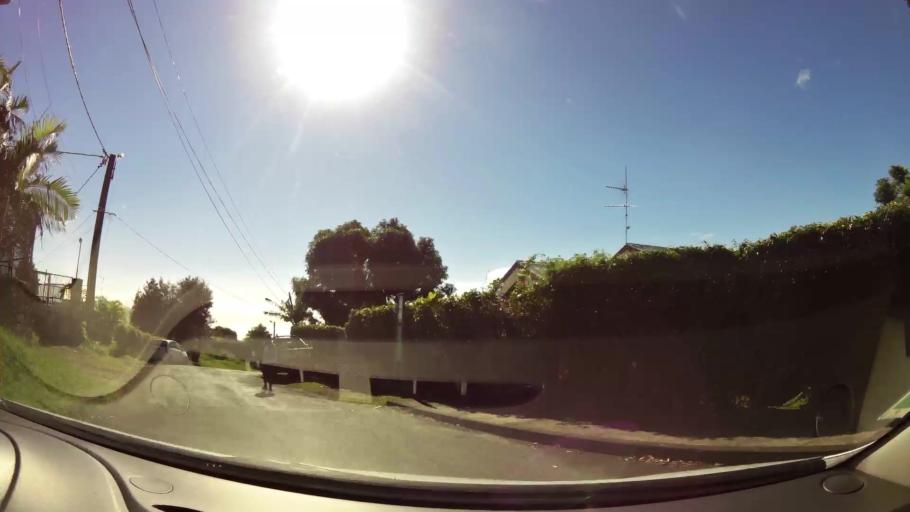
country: RE
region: Reunion
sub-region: Reunion
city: Saint-Denis
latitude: -20.9190
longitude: 55.4859
